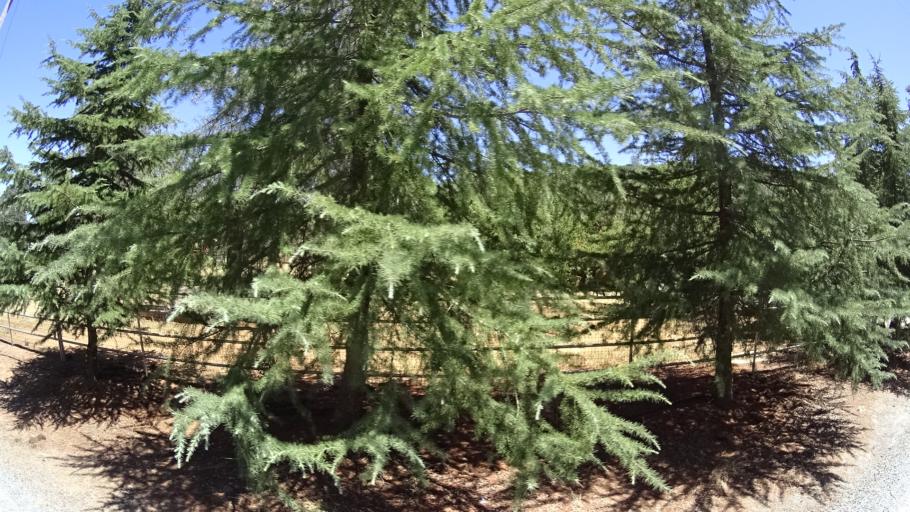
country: US
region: California
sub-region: Calaveras County
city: Copperopolis
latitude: 38.0624
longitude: -120.6541
